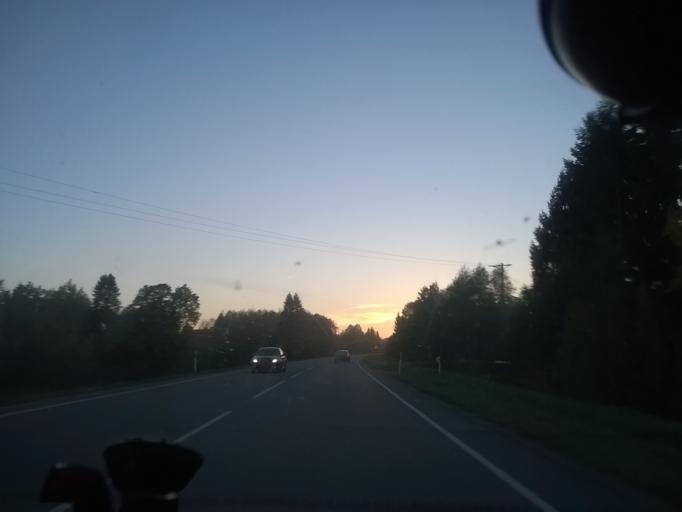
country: EE
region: Laeaene
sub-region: Ridala Parish
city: Uuemoisa
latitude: 58.9597
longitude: 23.8161
